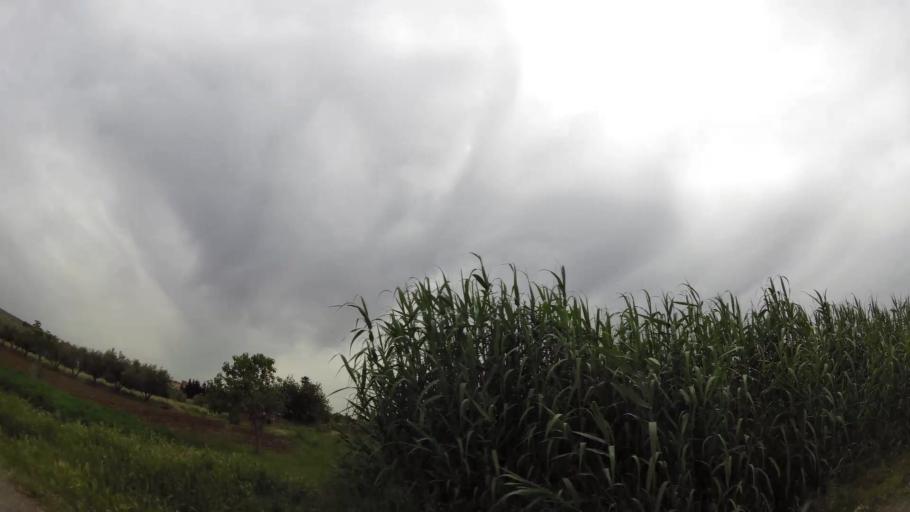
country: MA
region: Rabat-Sale-Zemmour-Zaer
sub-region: Khemisset
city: Khemisset
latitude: 33.7535
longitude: -6.1987
